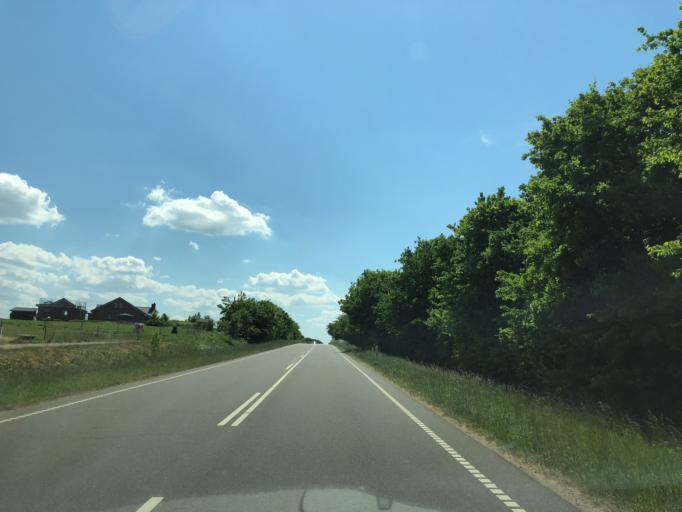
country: DK
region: Central Jutland
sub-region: Struer Kommune
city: Struer
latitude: 56.4836
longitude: 8.5557
